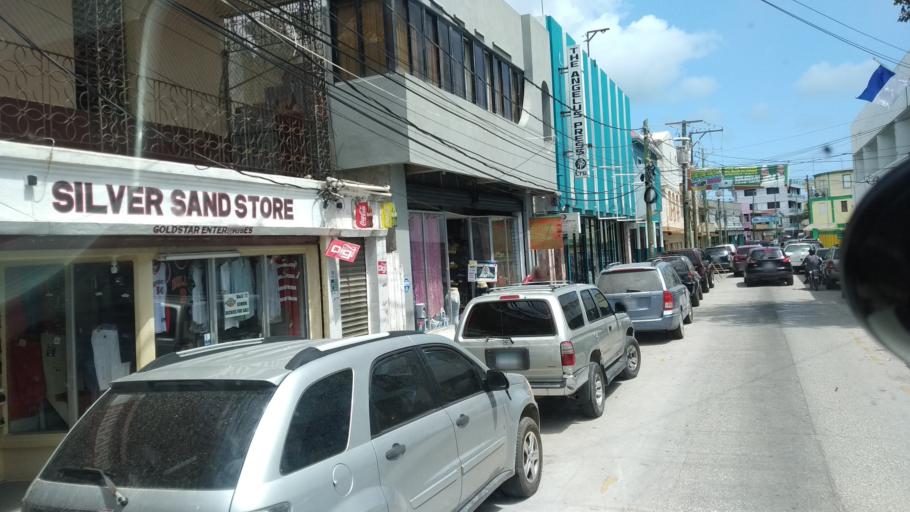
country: BZ
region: Belize
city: Belize City
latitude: 17.4960
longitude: -88.1864
